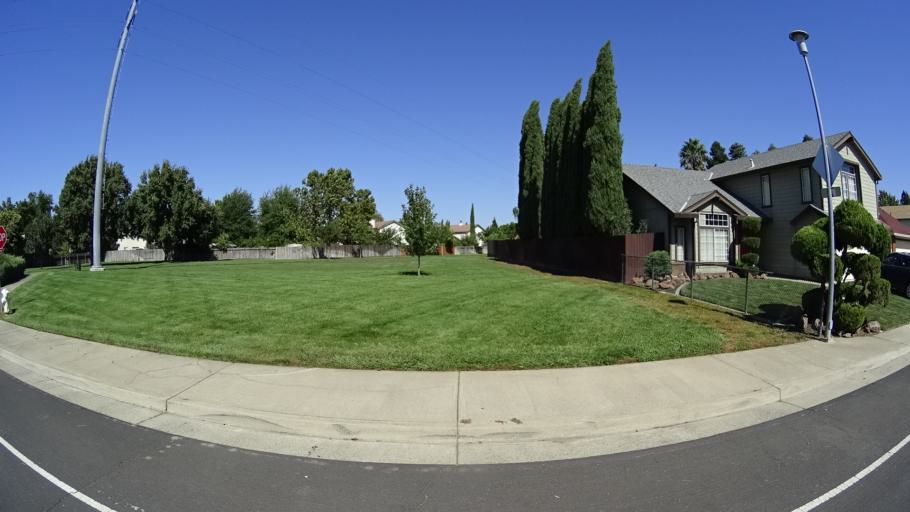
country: US
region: California
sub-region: Sacramento County
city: Laguna
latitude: 38.4301
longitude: -121.4398
